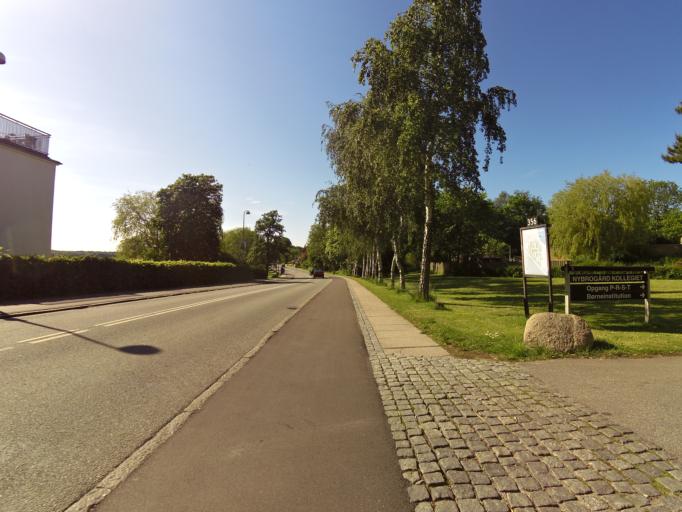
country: DK
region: Capital Region
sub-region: Gladsaxe Municipality
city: Buddinge
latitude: 55.7729
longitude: 12.4725
